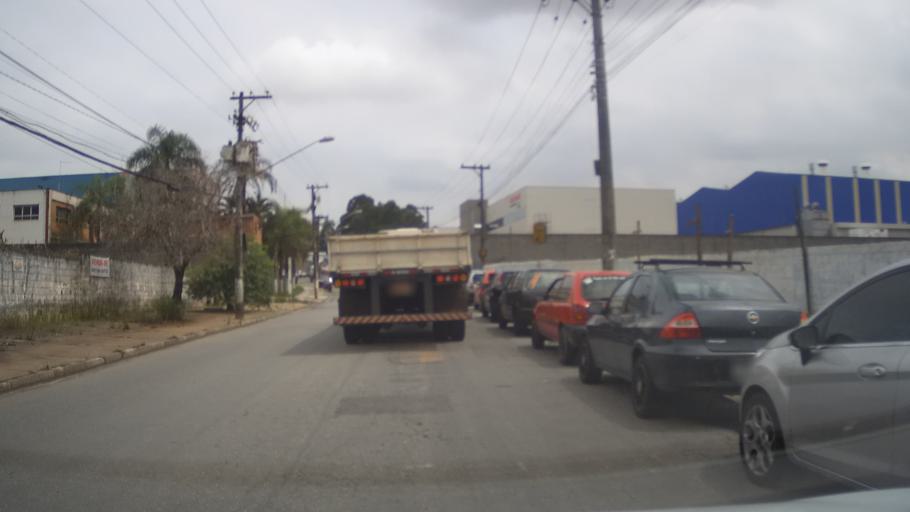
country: BR
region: Sao Paulo
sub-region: Itaquaquecetuba
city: Itaquaquecetuba
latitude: -23.4277
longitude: -46.3943
